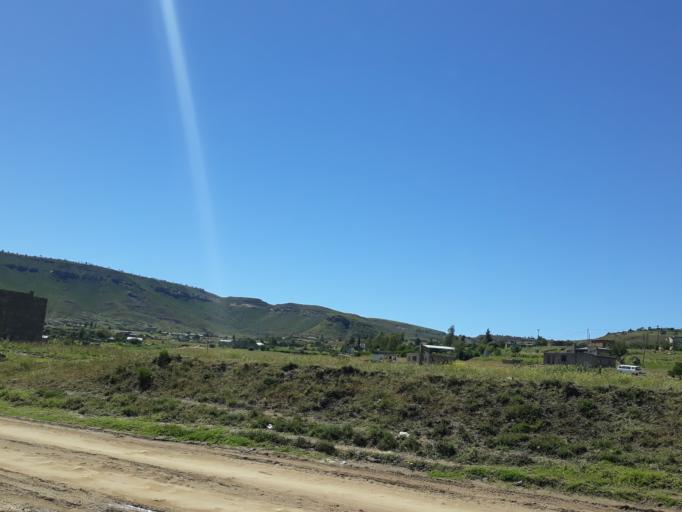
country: LS
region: Mohale's Hoek District
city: Mohale's Hoek
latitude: -30.1131
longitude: 27.4708
